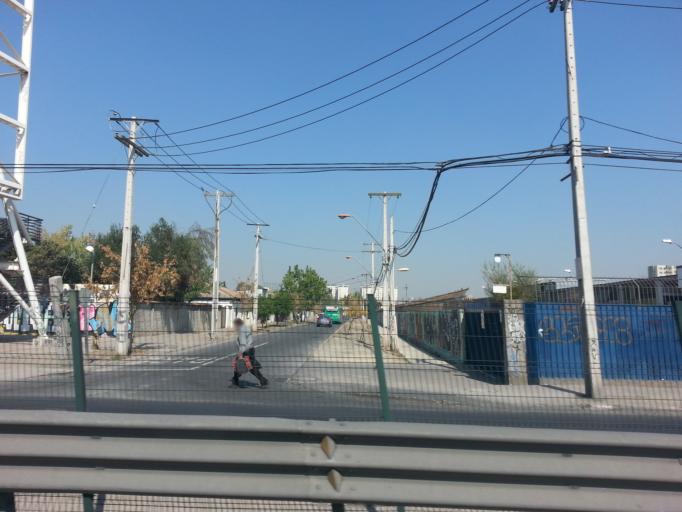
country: CL
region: Santiago Metropolitan
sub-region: Provincia de Santiago
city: La Pintana
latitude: -33.5395
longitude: -70.6556
